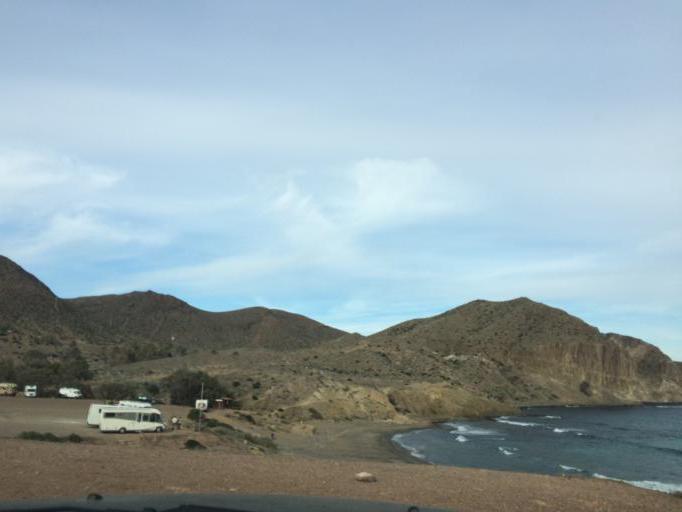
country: ES
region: Andalusia
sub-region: Provincia de Almeria
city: San Jose
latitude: 36.8155
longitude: -2.0511
